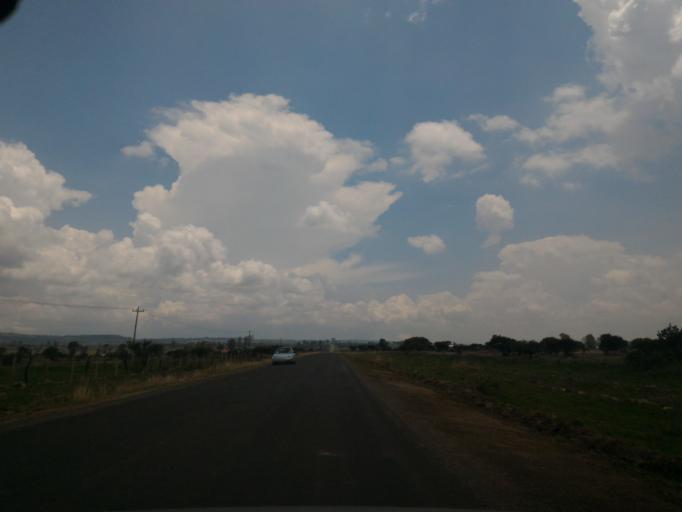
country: MX
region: Jalisco
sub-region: Arandas
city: Santiaguito (Santiaguito de Velazquez)
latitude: 20.8188
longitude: -102.1927
